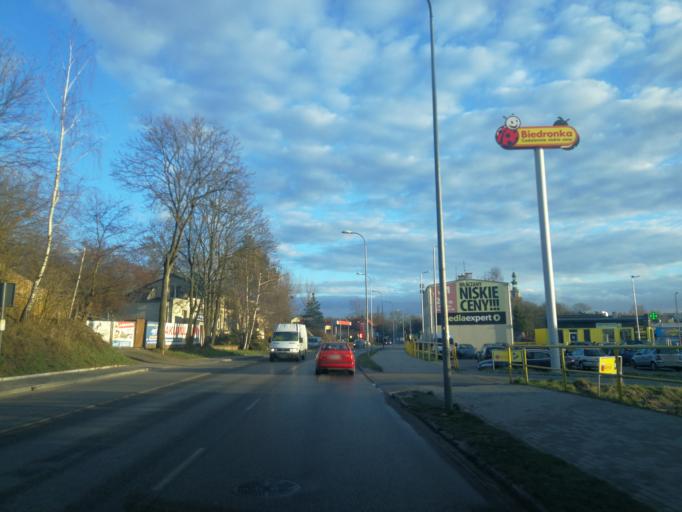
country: PL
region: Kujawsko-Pomorskie
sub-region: Powiat torunski
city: Chelmza
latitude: 53.1920
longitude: 18.6133
